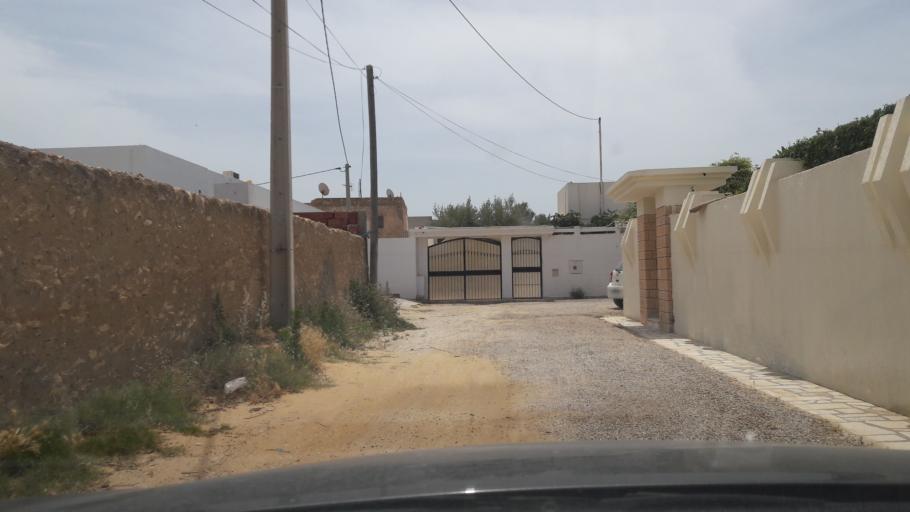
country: TN
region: Safaqis
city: Al Qarmadah
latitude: 34.7855
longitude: 10.7588
